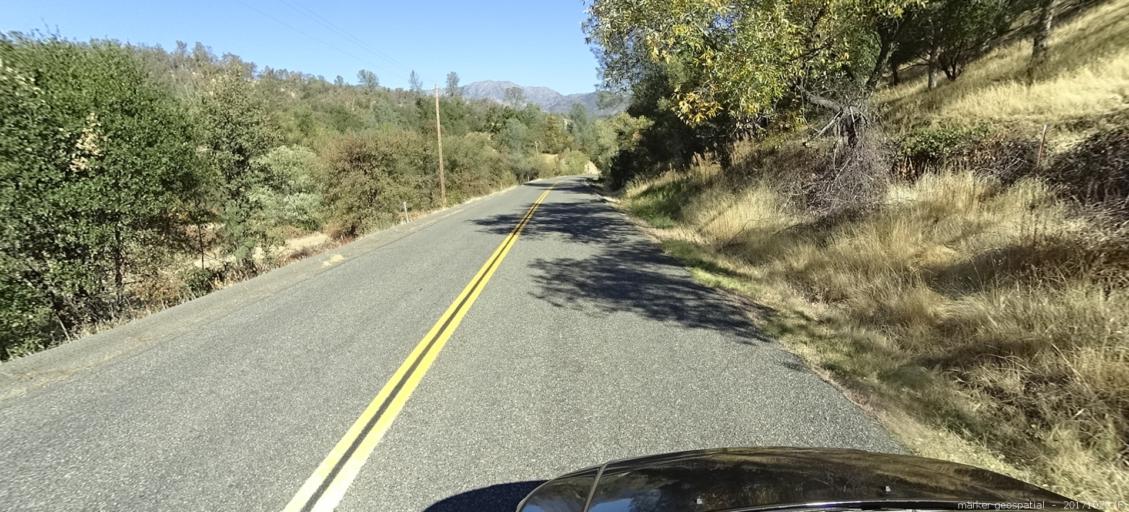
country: US
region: California
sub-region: Shasta County
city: Shasta
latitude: 40.4664
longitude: -122.6239
